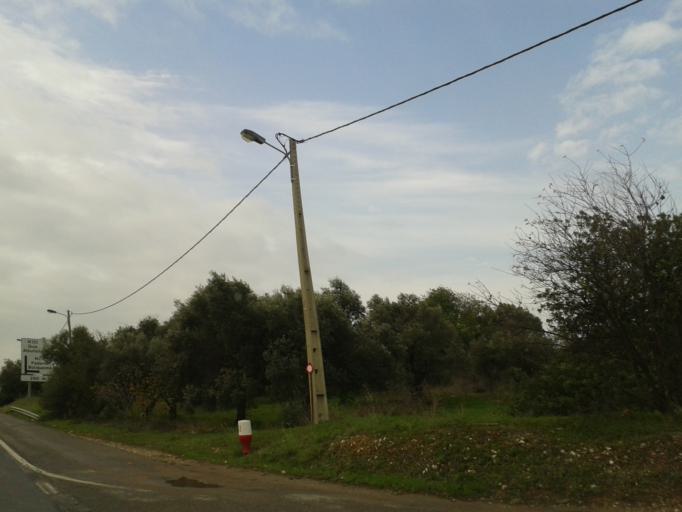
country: PT
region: Faro
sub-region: Loule
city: Boliqueime
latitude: 37.1283
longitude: -8.1570
